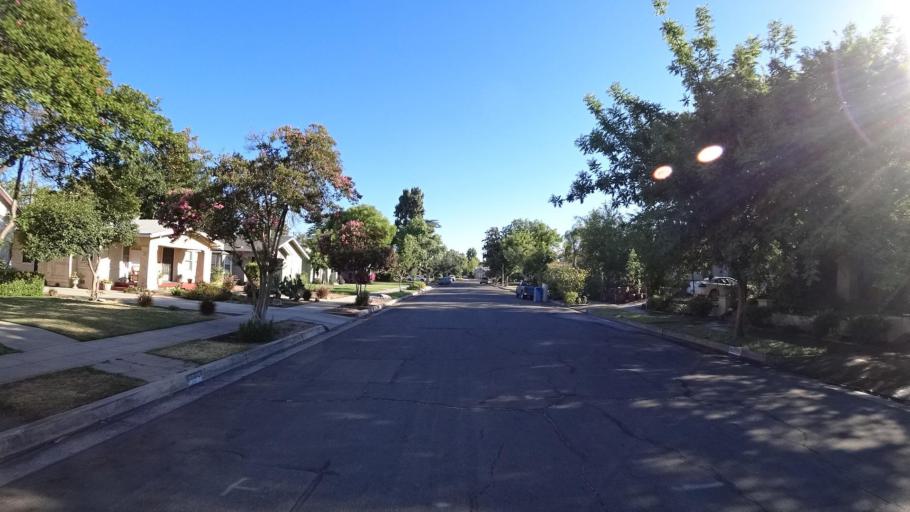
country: US
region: California
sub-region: Fresno County
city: Fresno
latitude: 36.7691
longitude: -119.8059
